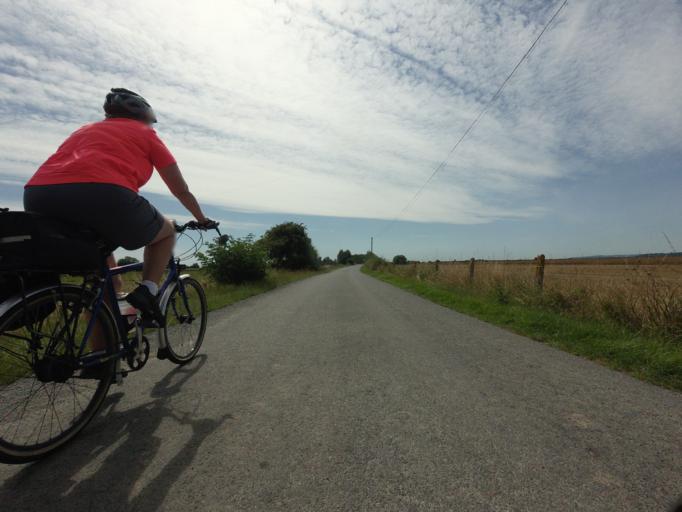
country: GB
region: England
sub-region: Kent
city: Stone
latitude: 51.0006
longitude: 0.8031
